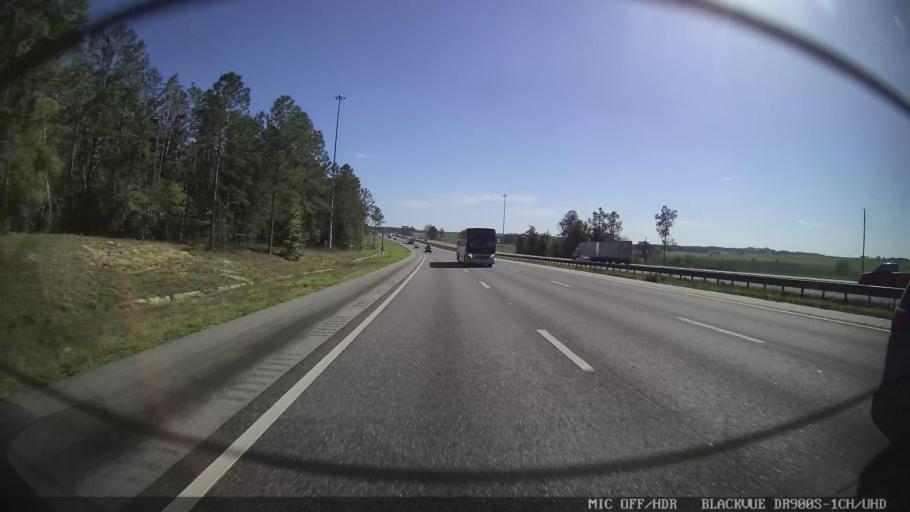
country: US
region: Florida
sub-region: Hernando County
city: Hill 'n Dale
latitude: 28.4991
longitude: -82.2469
